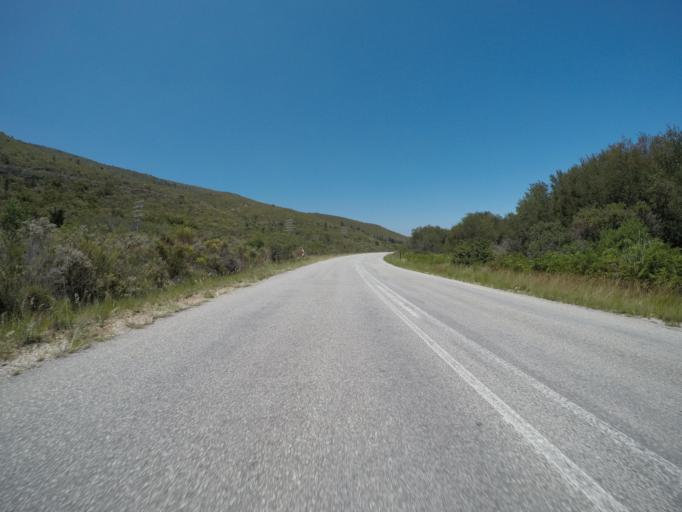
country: ZA
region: Eastern Cape
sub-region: Cacadu District Municipality
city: Kareedouw
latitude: -33.8680
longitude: 24.0260
